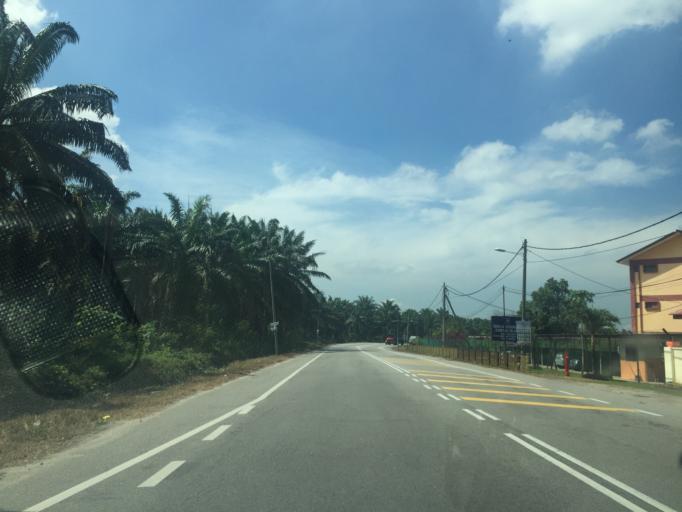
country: MY
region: Penang
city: Tasek Glugor
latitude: 5.4983
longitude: 100.5198
